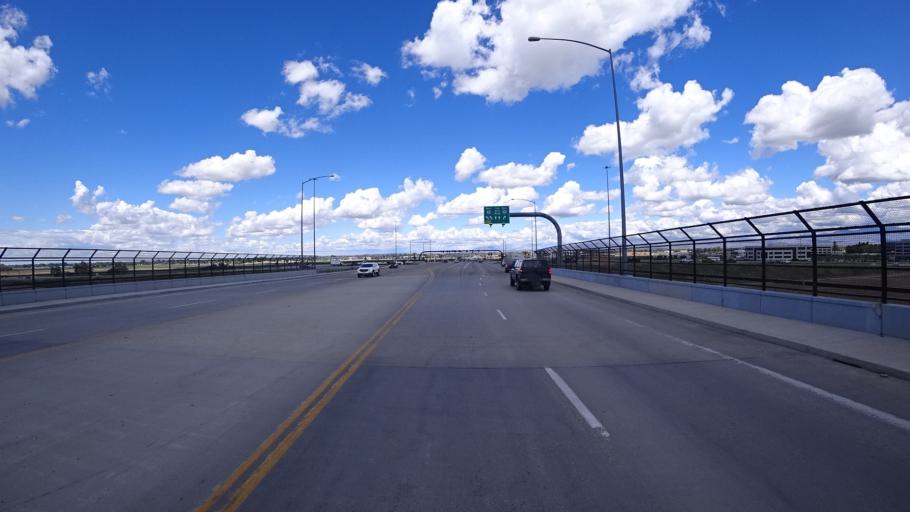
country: US
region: Idaho
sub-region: Ada County
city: Meridian
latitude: 43.5914
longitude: -116.4338
